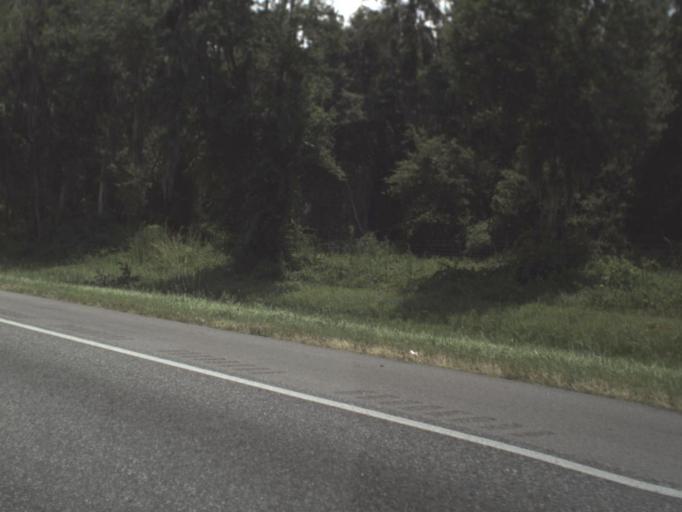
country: US
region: Florida
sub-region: Hamilton County
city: Jasper
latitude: 30.4394
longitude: -82.9182
